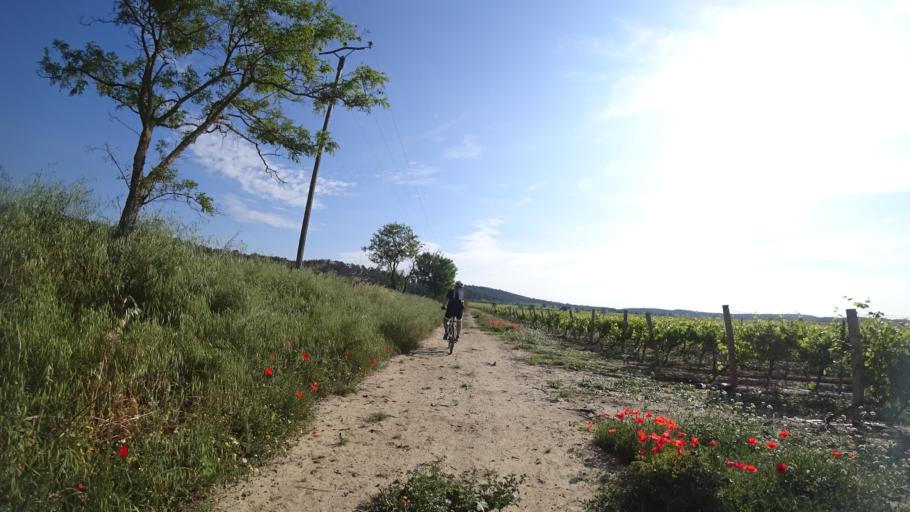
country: FR
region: Languedoc-Roussillon
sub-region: Departement de l'Herault
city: Olonzac
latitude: 43.2388
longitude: 2.7136
